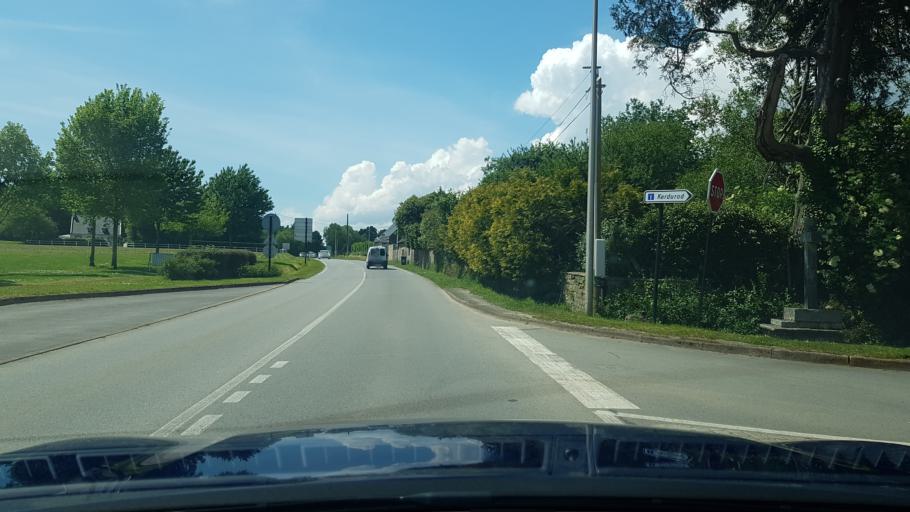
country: FR
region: Brittany
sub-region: Departement du Morbihan
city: Gestel
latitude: 47.8051
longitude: -3.4525
